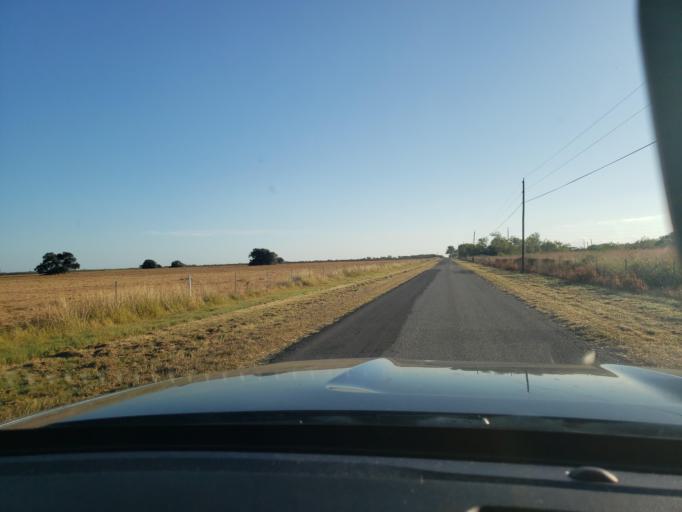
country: US
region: Texas
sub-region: Bee County
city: Beeville
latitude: 28.4288
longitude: -97.6943
